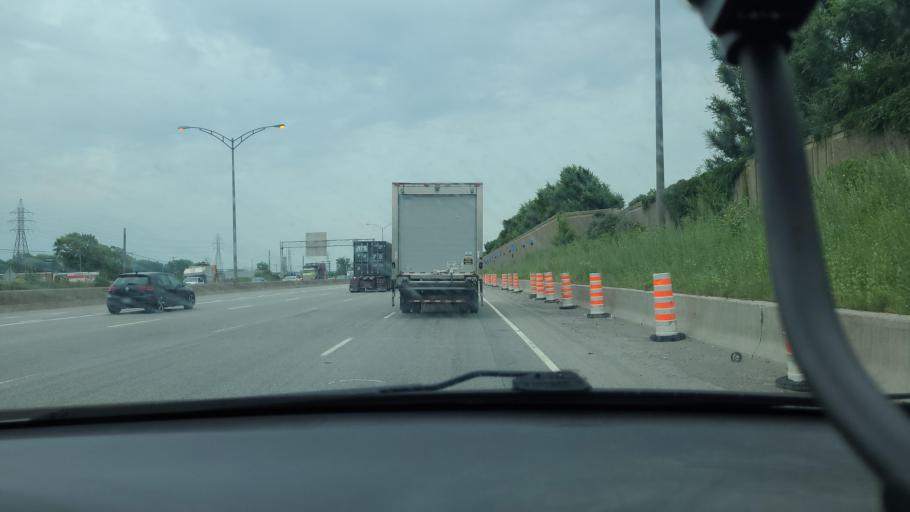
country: CA
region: Quebec
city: Cote-Saint-Luc
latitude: 45.4473
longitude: -73.6845
